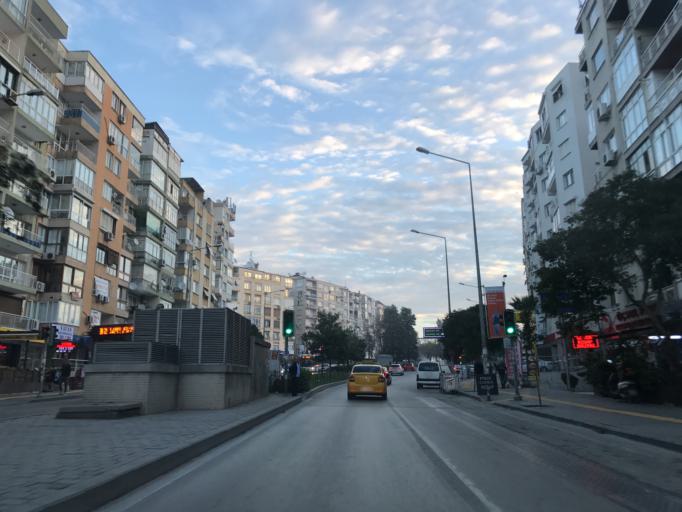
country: TR
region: Izmir
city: Izmir
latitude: 38.4051
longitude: 27.1199
